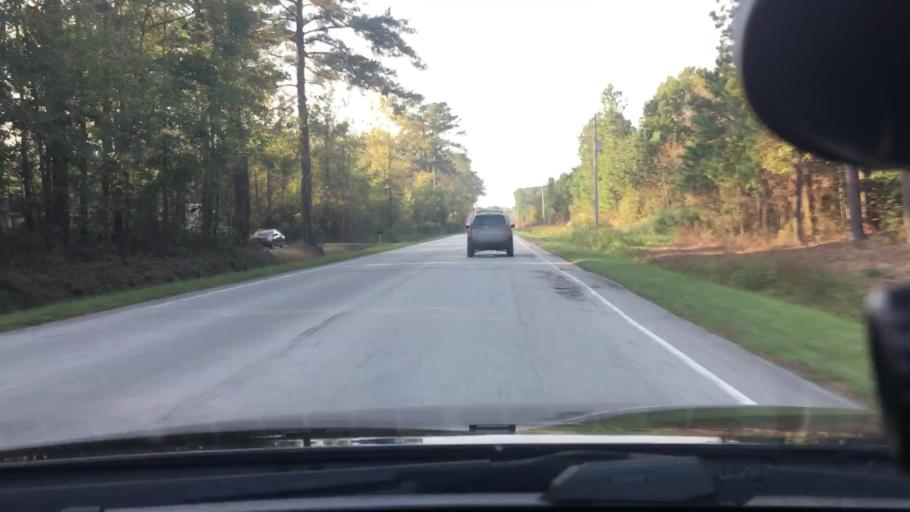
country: US
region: North Carolina
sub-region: Craven County
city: Vanceboro
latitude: 35.4118
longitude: -77.2484
